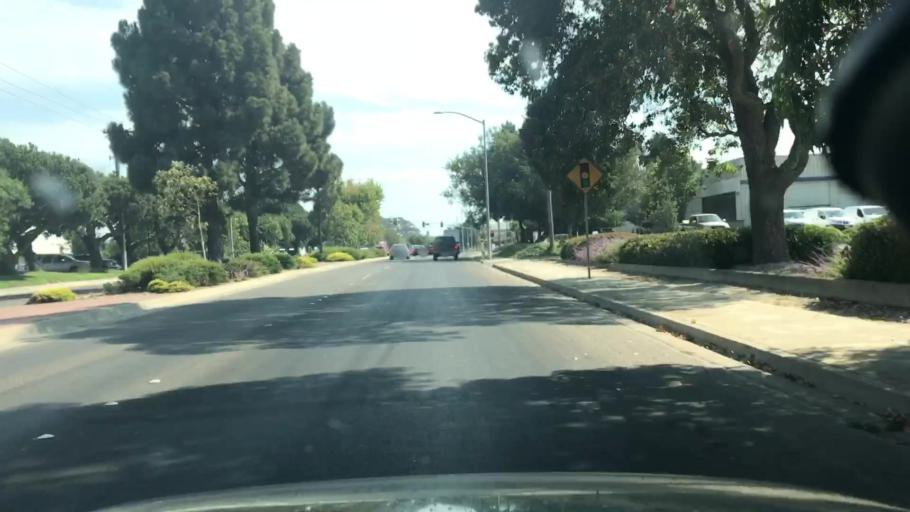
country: US
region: California
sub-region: Santa Barbara County
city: Santa Maria
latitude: 34.9225
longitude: -120.4540
